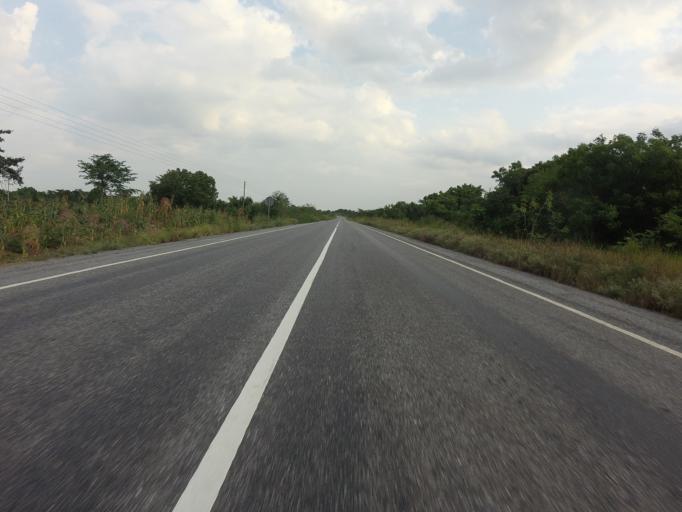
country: GH
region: Volta
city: Ho
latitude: 6.3588
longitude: 0.5365
